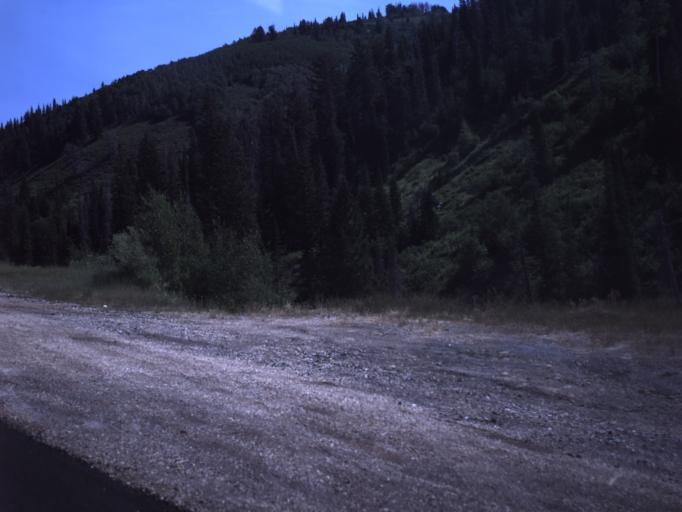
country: US
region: Utah
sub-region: Sanpete County
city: Fairview
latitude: 39.6581
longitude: -111.3518
